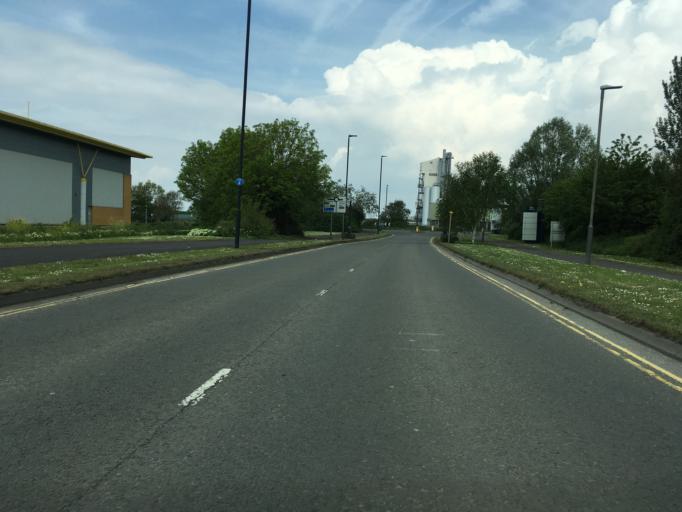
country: GB
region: England
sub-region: South Gloucestershire
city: Severn Beach
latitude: 51.5236
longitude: -2.6831
